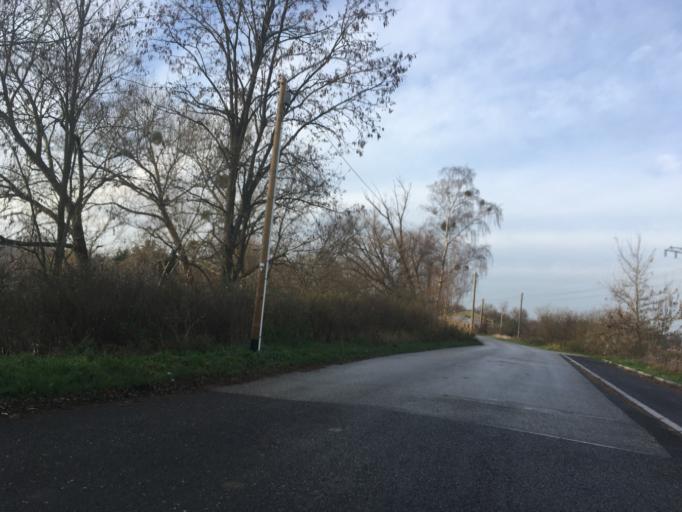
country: DE
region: Brandenburg
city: Bad Freienwalde
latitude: 52.7939
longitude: 14.0371
